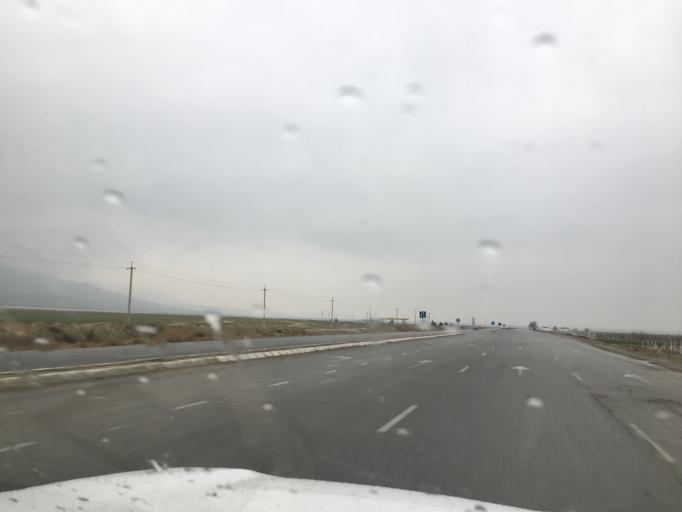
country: TM
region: Ahal
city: Annau
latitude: 37.7916
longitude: 58.8231
